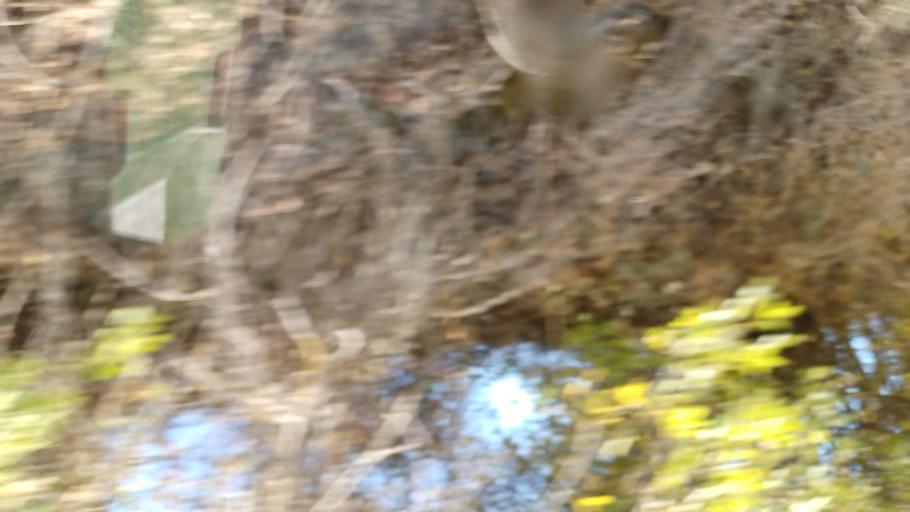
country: CY
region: Pafos
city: Tala
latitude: 34.9303
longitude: 32.4854
